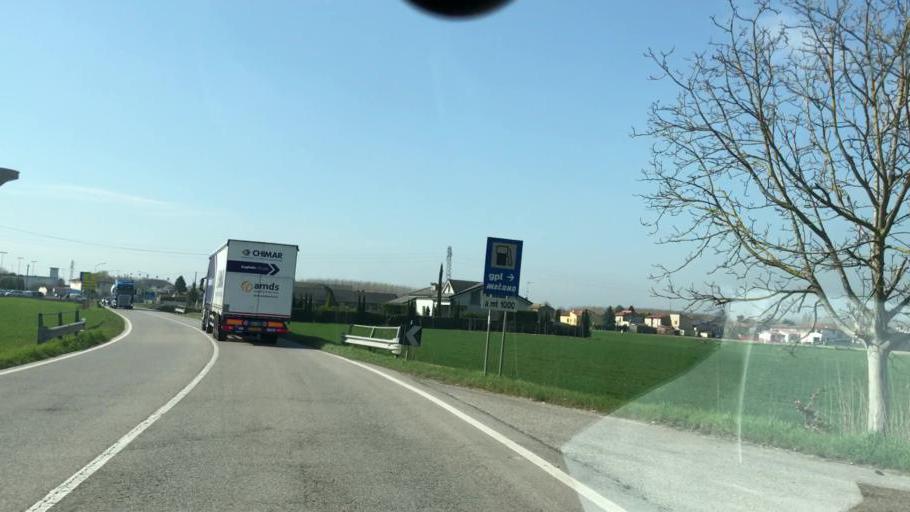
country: IT
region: Veneto
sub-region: Provincia di Rovigo
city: Castelnovo Bariano
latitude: 45.0274
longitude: 11.2967
